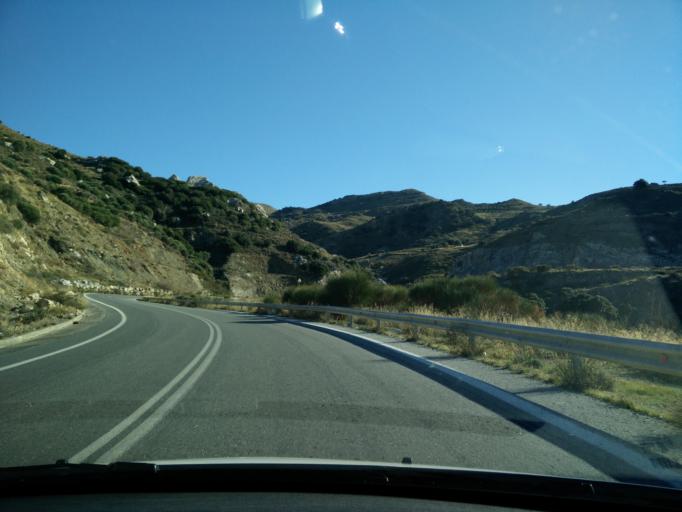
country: GR
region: Crete
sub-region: Nomos Irakleiou
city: Arkalochori
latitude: 35.0709
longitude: 25.3597
